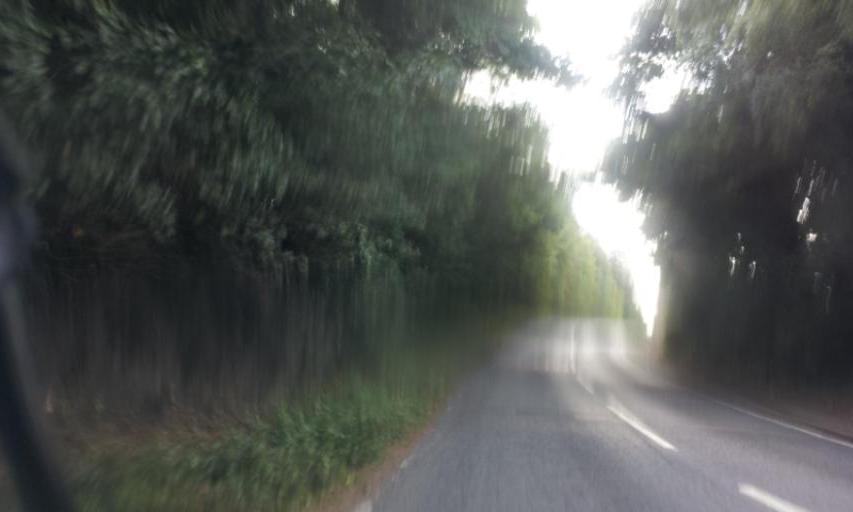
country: GB
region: England
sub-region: Kent
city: Boxley
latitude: 51.2930
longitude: 0.5392
